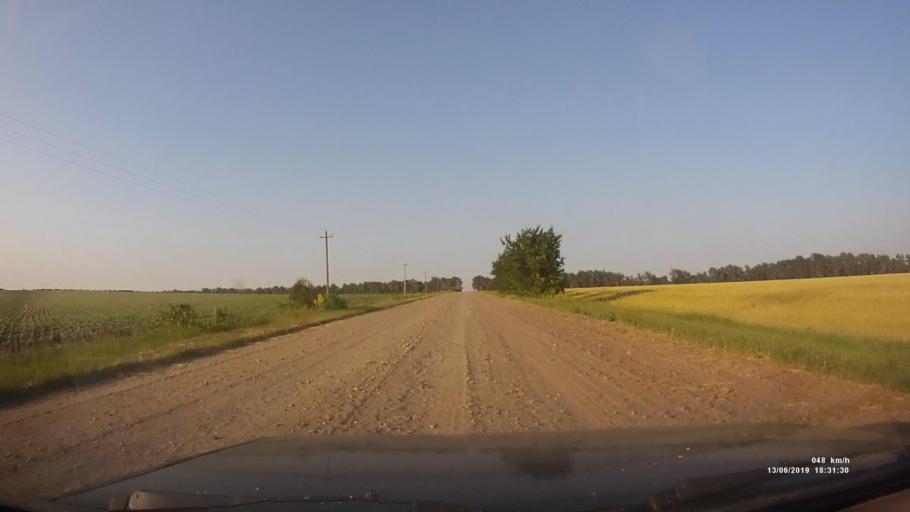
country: RU
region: Rostov
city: Kazanskaya
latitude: 49.8665
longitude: 41.3594
